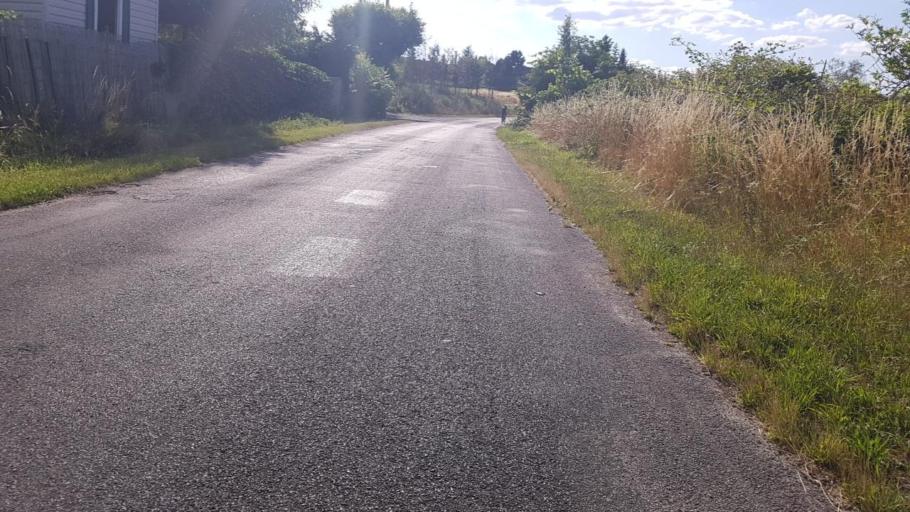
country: FR
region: Picardie
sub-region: Departement de l'Oise
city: Senlis
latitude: 49.1972
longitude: 2.5993
